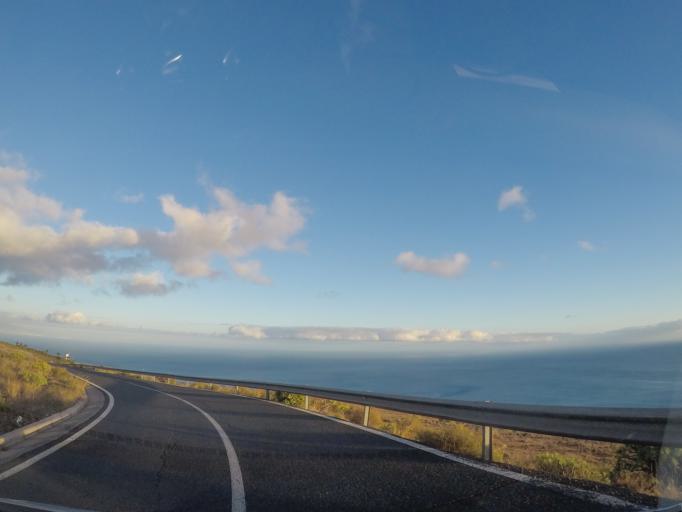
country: ES
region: Canary Islands
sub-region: Provincia de Santa Cruz de Tenerife
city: Alajero
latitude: 28.0451
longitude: -17.2335
